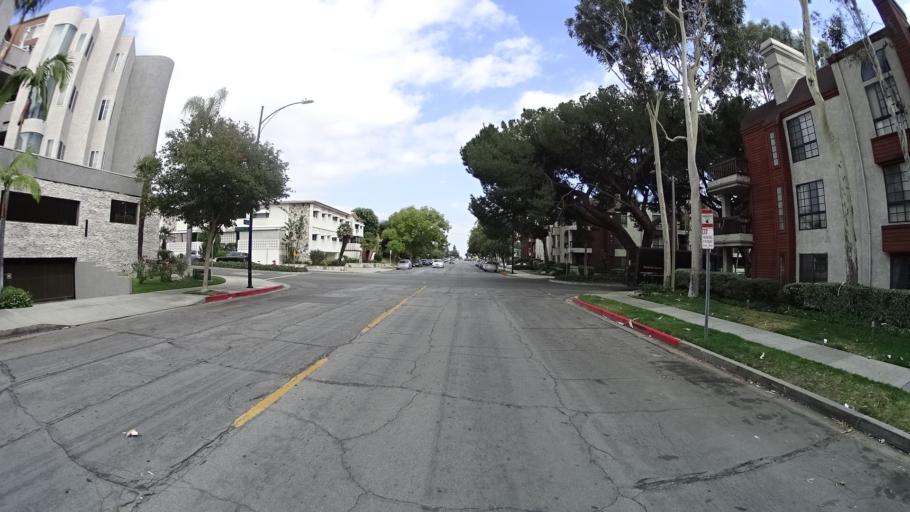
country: US
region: California
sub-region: Los Angeles County
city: Burbank
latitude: 34.1907
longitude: -118.3194
